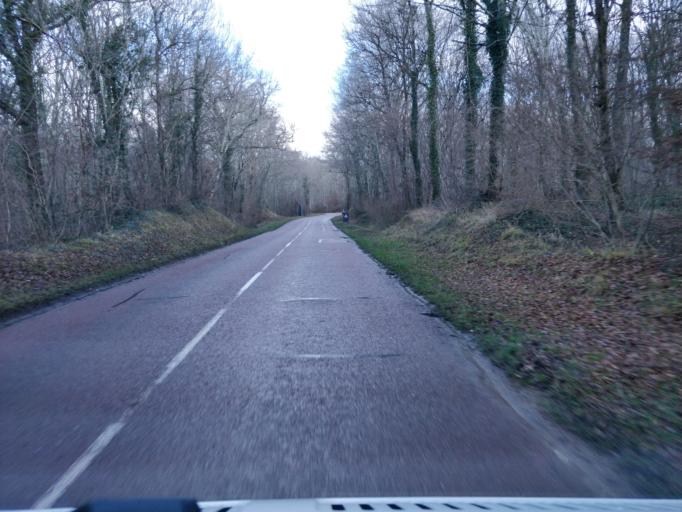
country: FR
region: Centre
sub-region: Departement du Loir-et-Cher
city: Saint-Dye-sur-Loire
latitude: 47.6203
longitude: 1.5075
